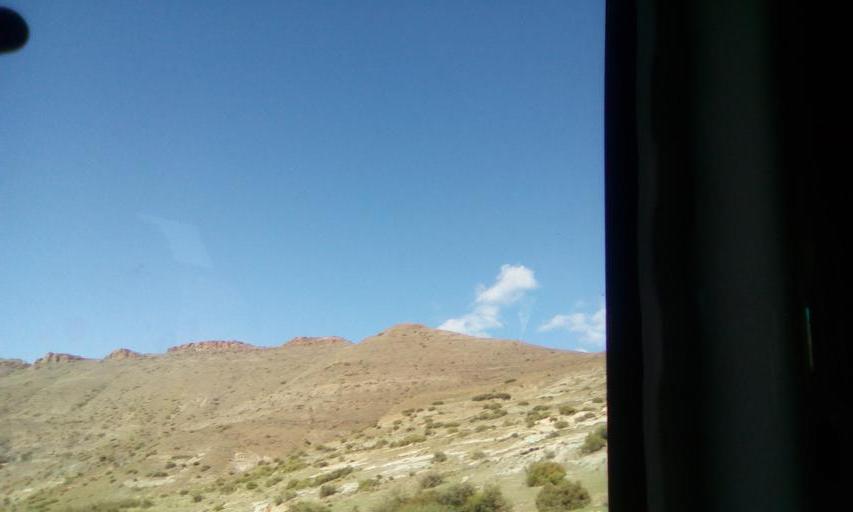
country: LS
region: Qacha's Nek
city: Qacha's Nek
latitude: -30.0572
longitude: 28.2866
